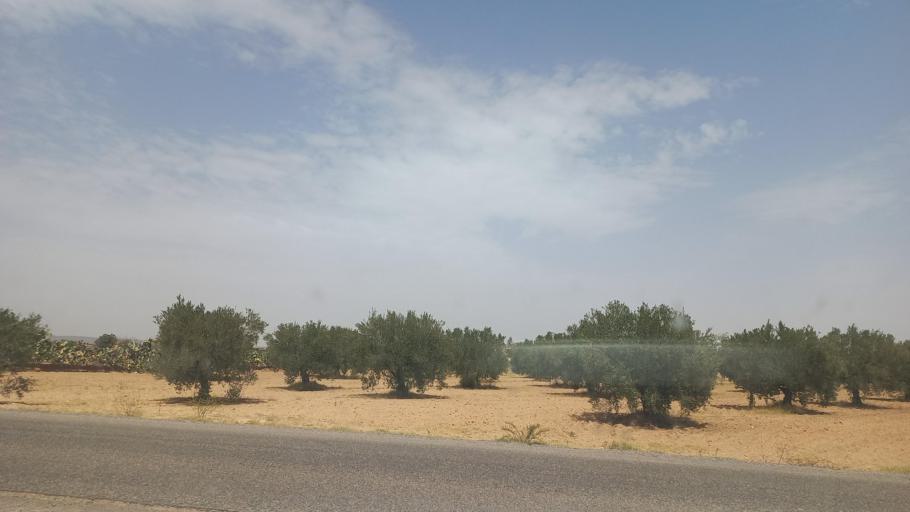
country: TN
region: Al Qasrayn
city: Kasserine
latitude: 35.2677
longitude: 8.9851
